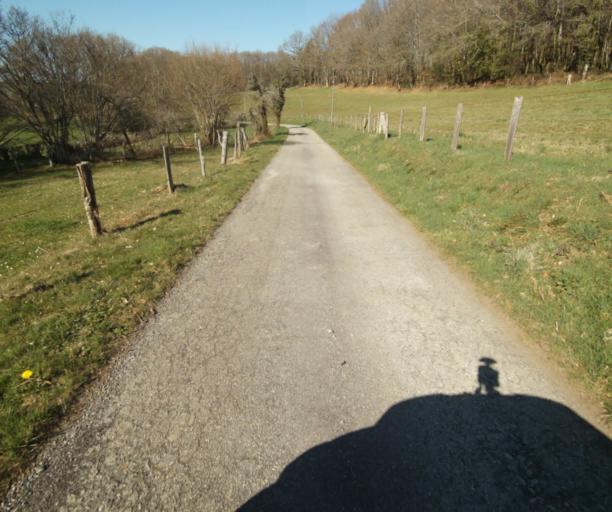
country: FR
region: Limousin
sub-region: Departement de la Correze
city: Chamboulive
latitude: 45.4845
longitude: 1.7437
